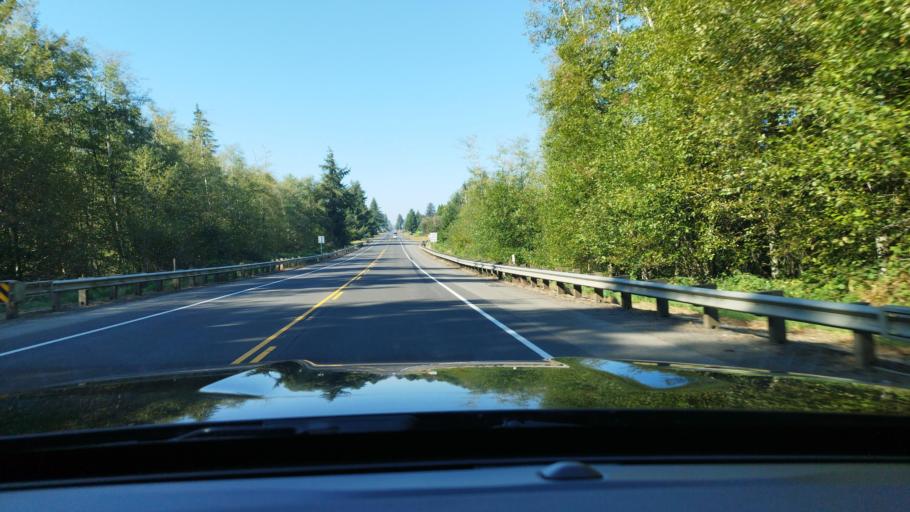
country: US
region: Washington
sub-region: Wahkiakum County
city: Cathlamet
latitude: 46.1691
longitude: -123.5677
